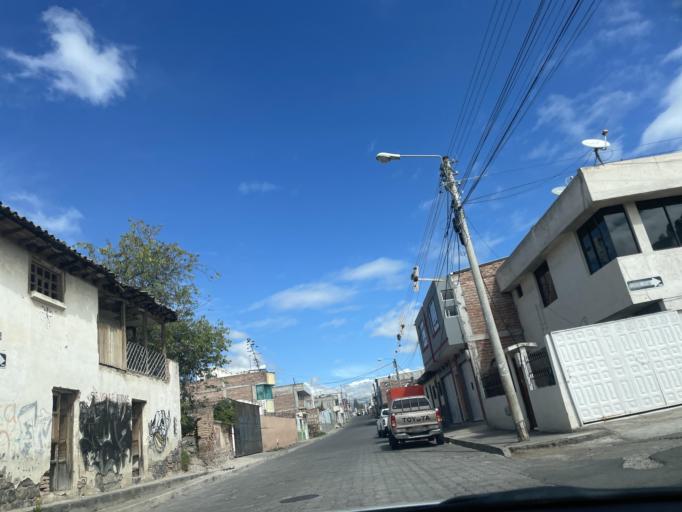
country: EC
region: Chimborazo
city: Guano
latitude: -1.6069
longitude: -78.6359
